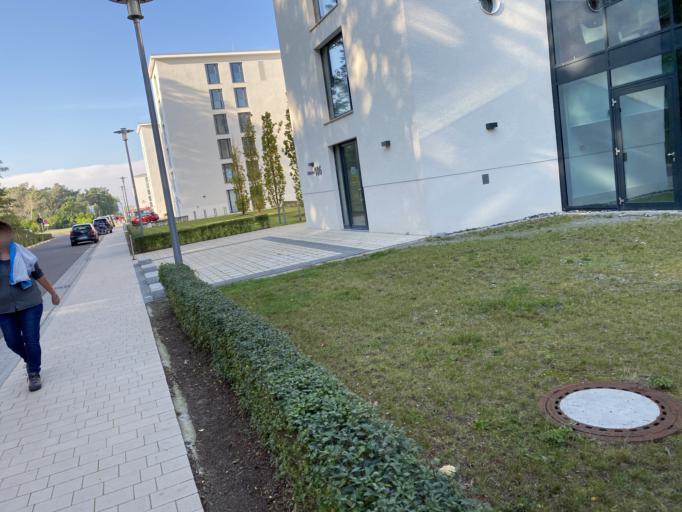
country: DE
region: Mecklenburg-Vorpommern
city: Ostseebad Binz
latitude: 54.4290
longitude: 13.5817
